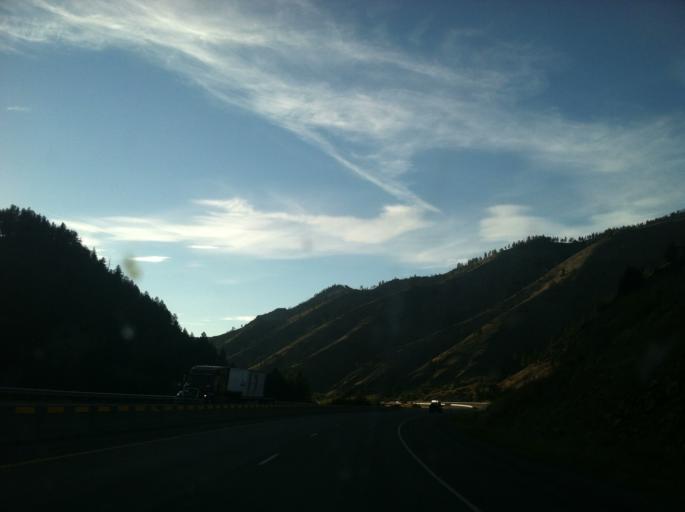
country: US
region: Montana
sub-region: Missoula County
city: Clinton
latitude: 46.7017
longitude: -113.4502
